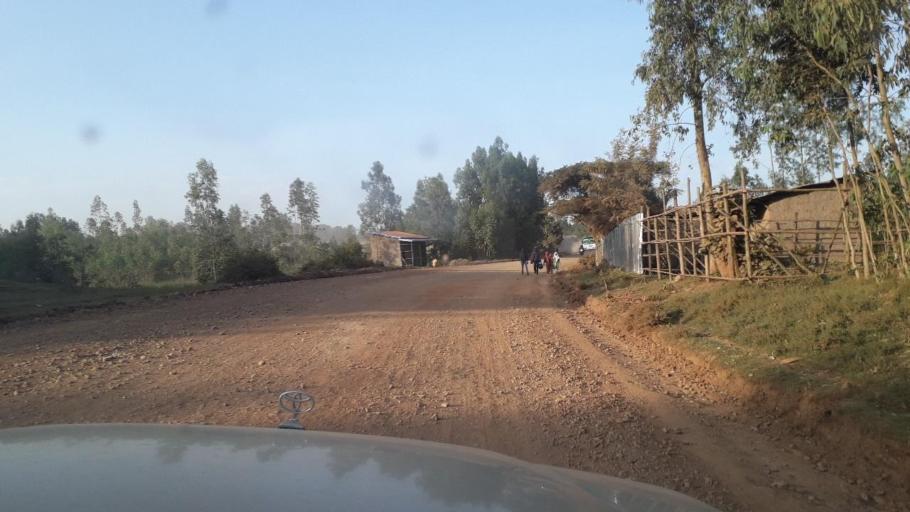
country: ET
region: Oromiya
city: Jima
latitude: 7.6187
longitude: 36.8344
